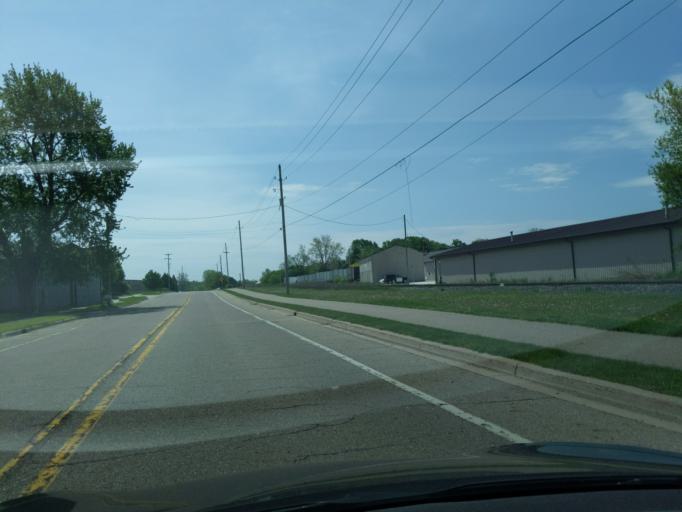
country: US
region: Michigan
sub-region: Ingham County
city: Holt
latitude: 42.6457
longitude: -84.5068
